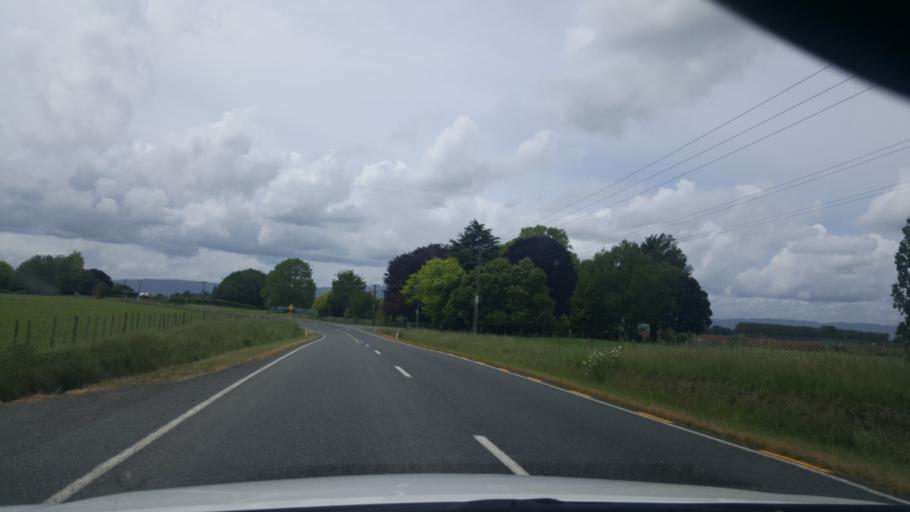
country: NZ
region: Waikato
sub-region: Matamata-Piako District
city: Matamata
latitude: -37.8757
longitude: 175.7220
